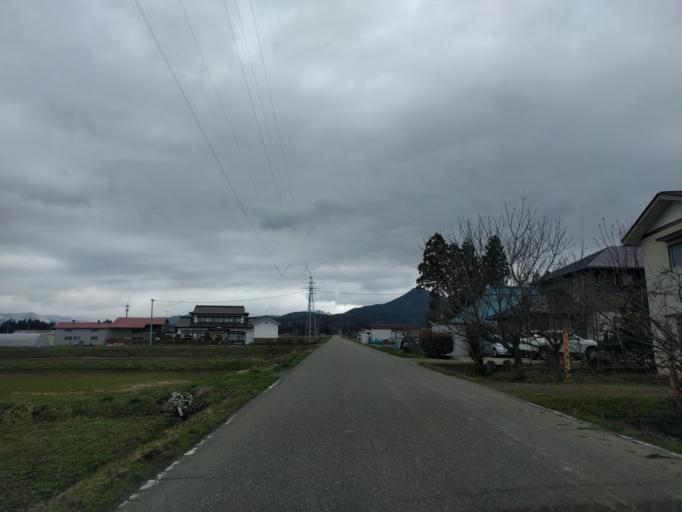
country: JP
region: Fukushima
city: Kitakata
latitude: 37.6587
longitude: 139.9129
